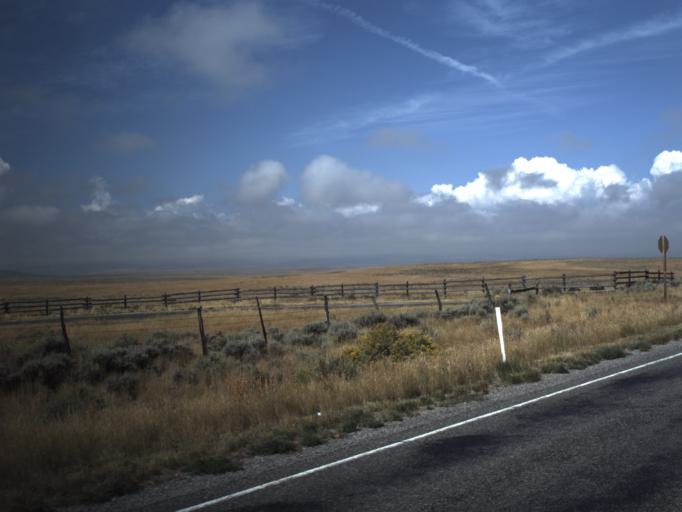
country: US
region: Wyoming
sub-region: Uinta County
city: Evanston
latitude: 41.4376
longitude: -111.0694
